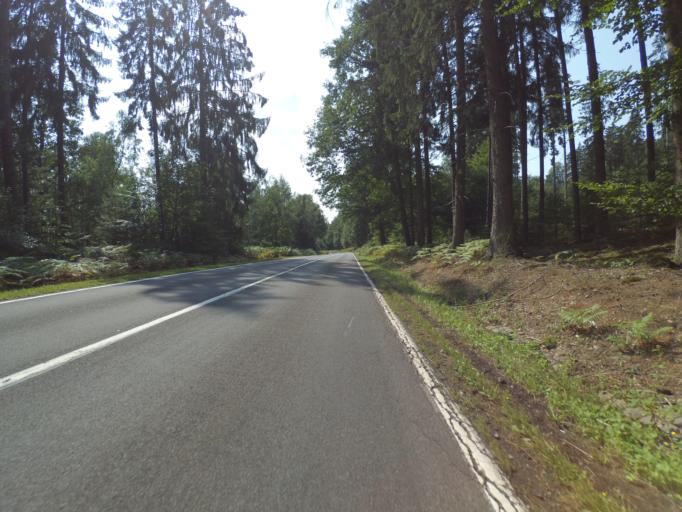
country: DE
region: Saarland
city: Britten
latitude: 49.5061
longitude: 6.6504
